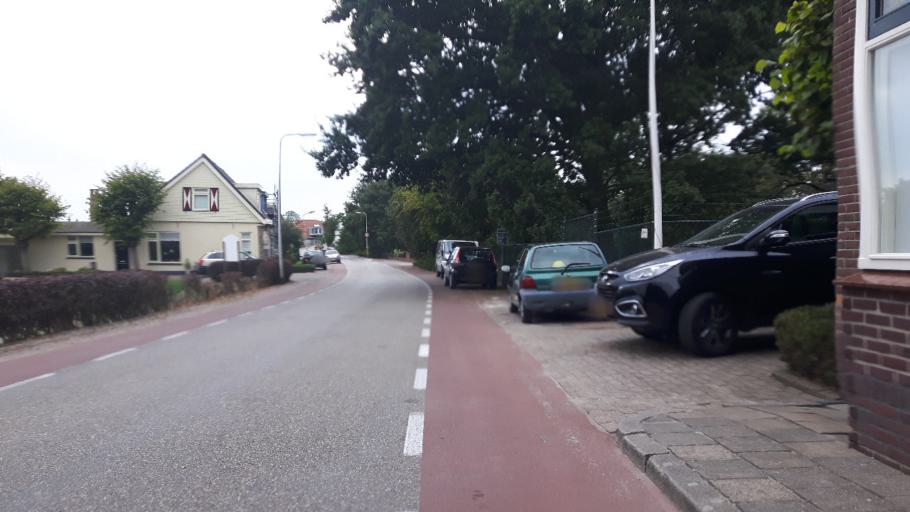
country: NL
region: South Holland
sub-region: Gemeente Hillegom
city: Hillegom
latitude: 52.3080
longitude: 4.5537
